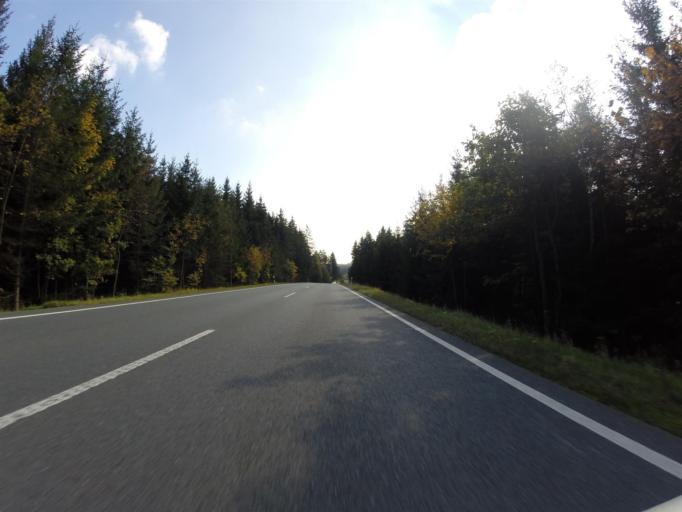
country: DE
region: Thuringia
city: Tanna
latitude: 50.4741
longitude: 11.8392
